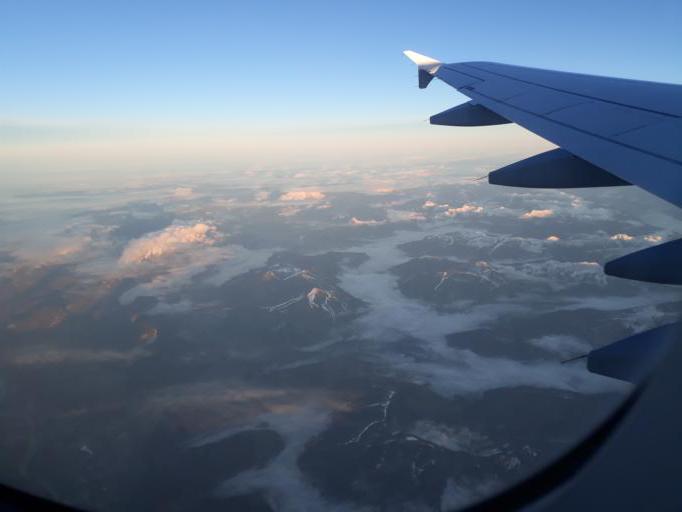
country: AT
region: Tyrol
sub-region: Politischer Bezirk Kufstein
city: Alpbach
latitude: 47.4210
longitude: 11.9369
